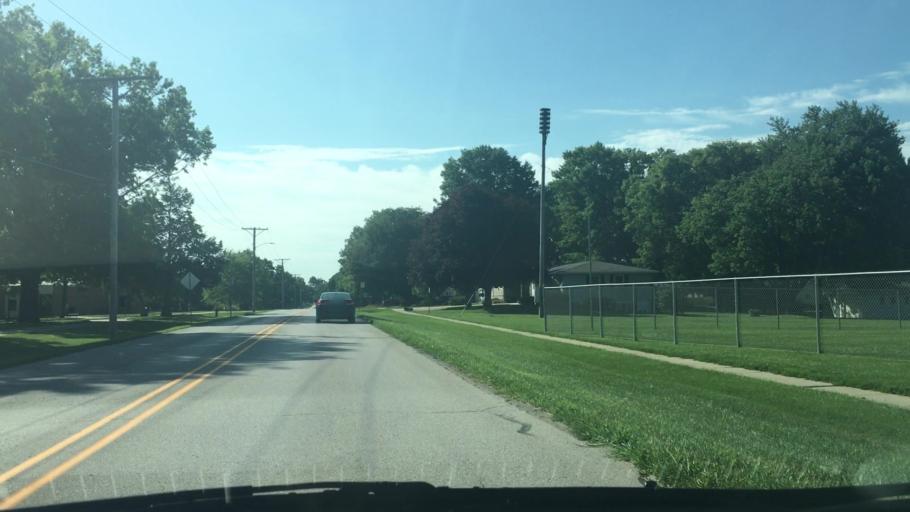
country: US
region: Iowa
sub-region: Johnson County
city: North Liberty
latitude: 41.7479
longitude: -91.5964
